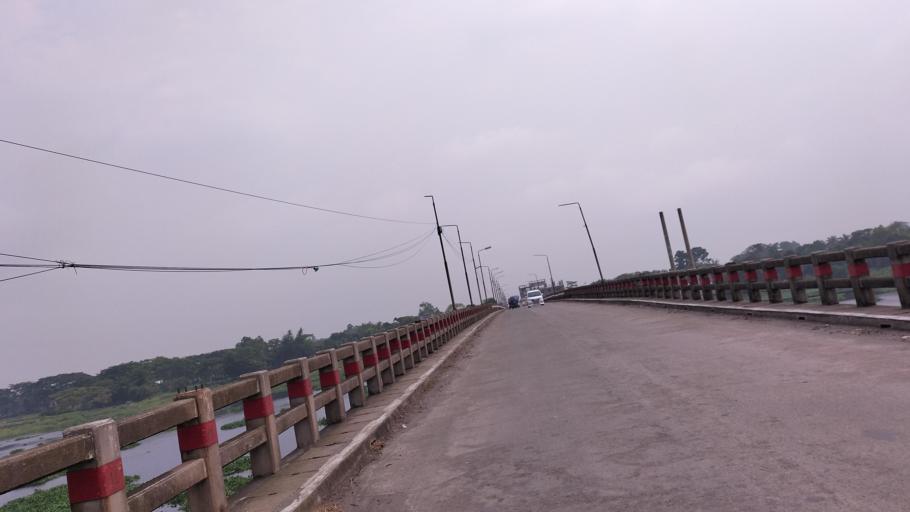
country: BD
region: Dhaka
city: Azimpur
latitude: 23.7555
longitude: 90.2495
